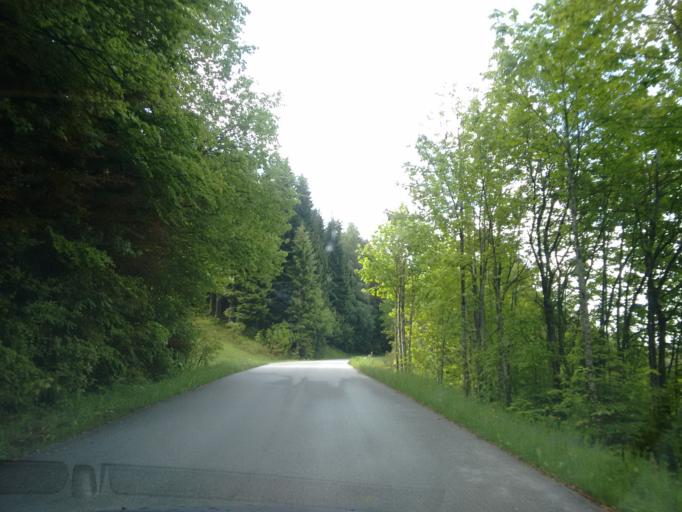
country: AT
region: Styria
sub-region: Politischer Bezirk Liezen
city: Altaussee
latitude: 47.6599
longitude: 13.7500
